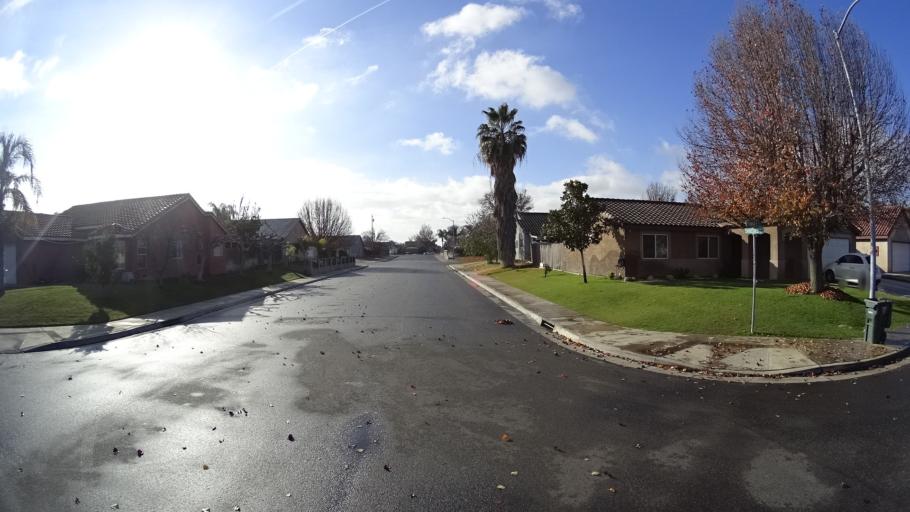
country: US
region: California
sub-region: Kern County
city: Greenfield
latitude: 35.2901
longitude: -119.0088
